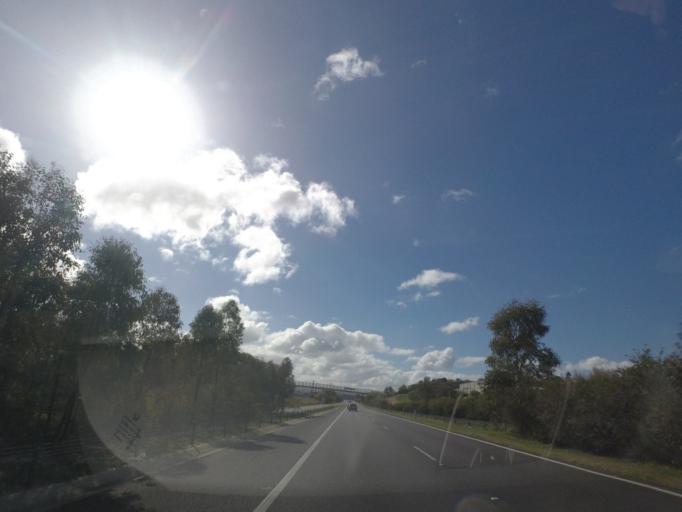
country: AU
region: New South Wales
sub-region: Albury Municipality
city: East Albury
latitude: -36.0901
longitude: 146.9242
